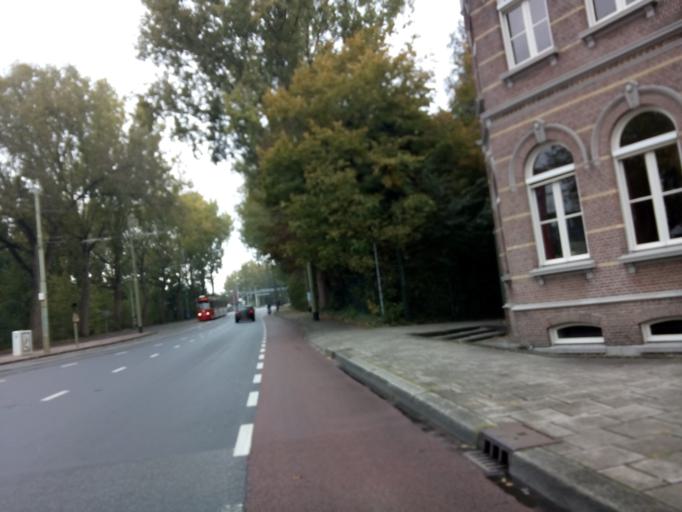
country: NL
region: South Holland
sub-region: Gemeente Delft
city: Delft
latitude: 52.0178
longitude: 4.3529
